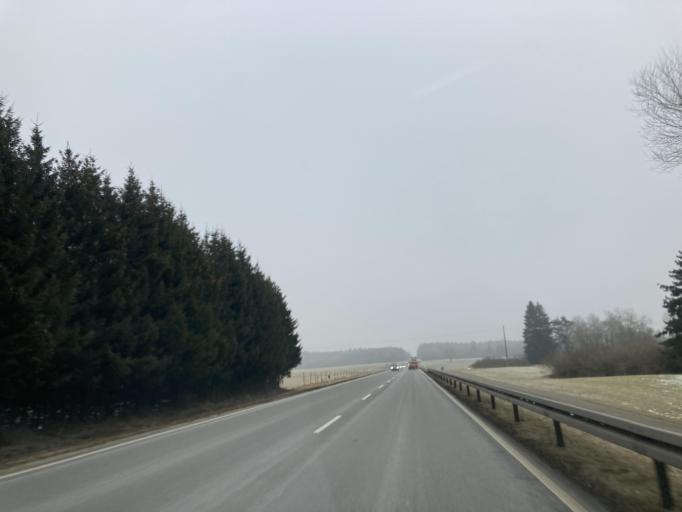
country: DE
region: Baden-Wuerttemberg
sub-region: Freiburg Region
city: Neuhausen ob Eck
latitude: 47.9771
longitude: 8.9602
